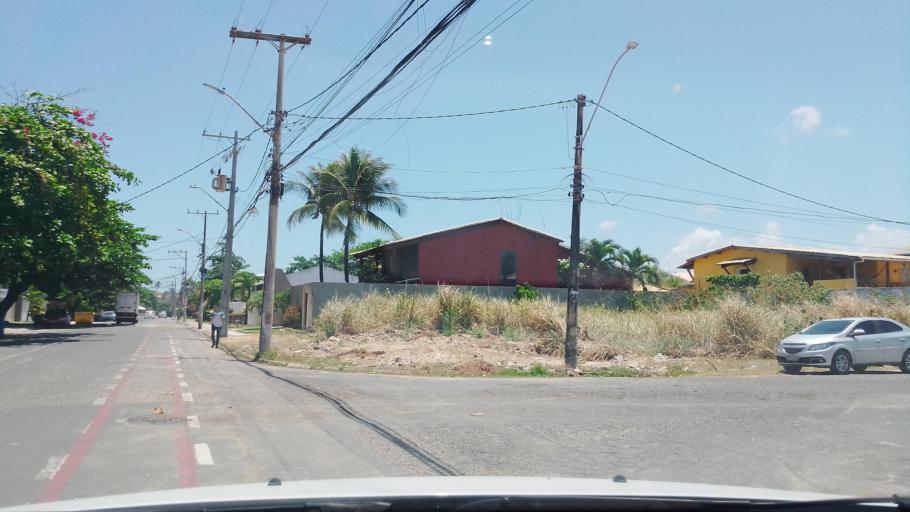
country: BR
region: Bahia
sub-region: Lauro De Freitas
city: Lauro de Freitas
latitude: -12.9322
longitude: -38.3239
